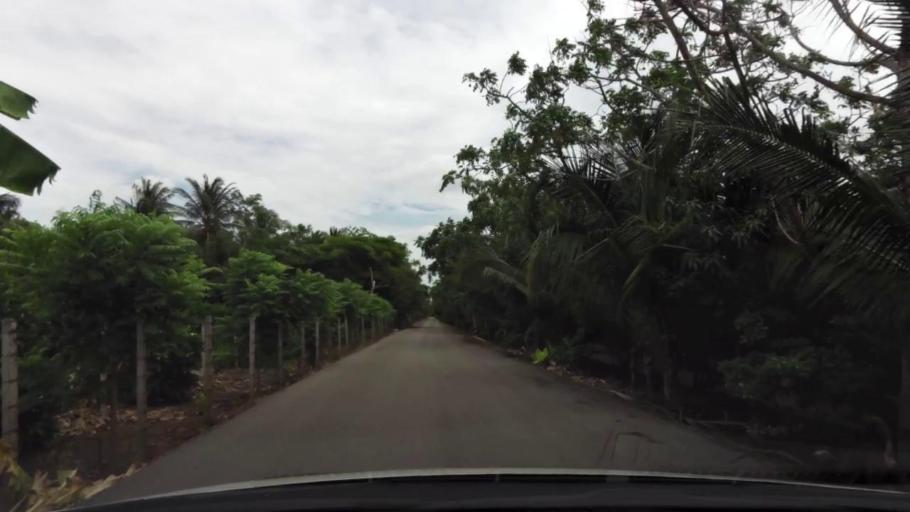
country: TH
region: Ratchaburi
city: Damnoen Saduak
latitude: 13.5524
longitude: 100.0031
